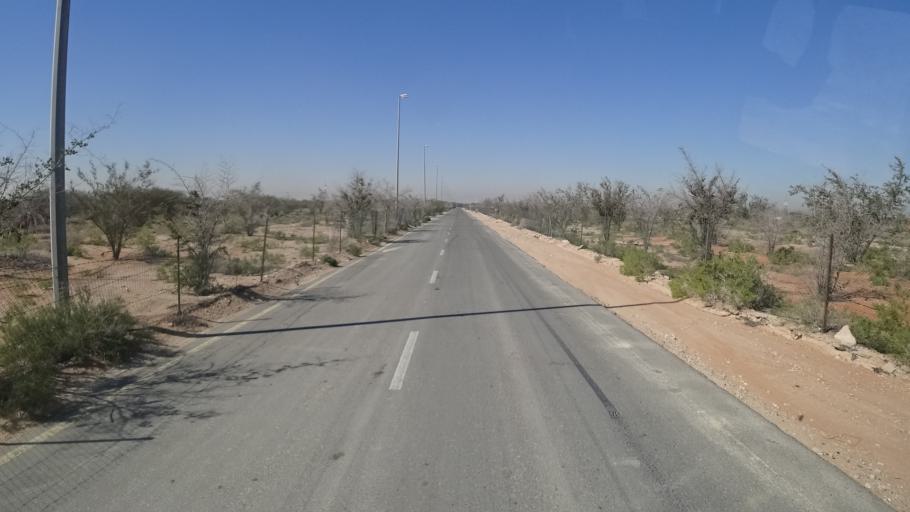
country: AE
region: Abu Dhabi
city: Al Ain
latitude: 24.1032
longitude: 55.7327
